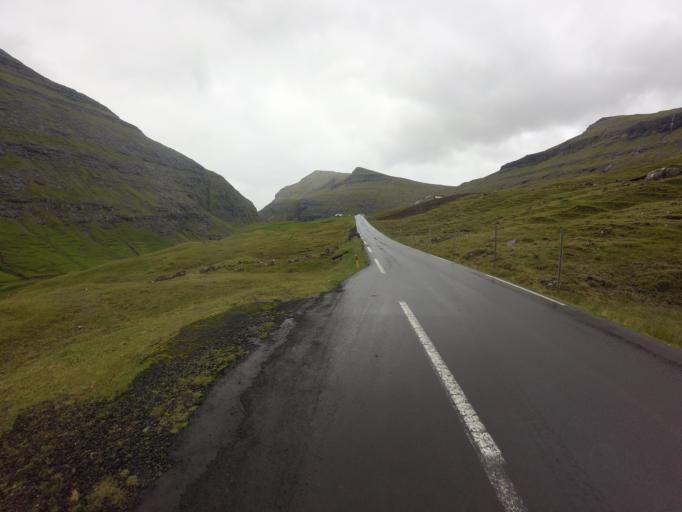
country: FO
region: Streymoy
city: Vestmanna
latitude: 62.2450
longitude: -7.1735
